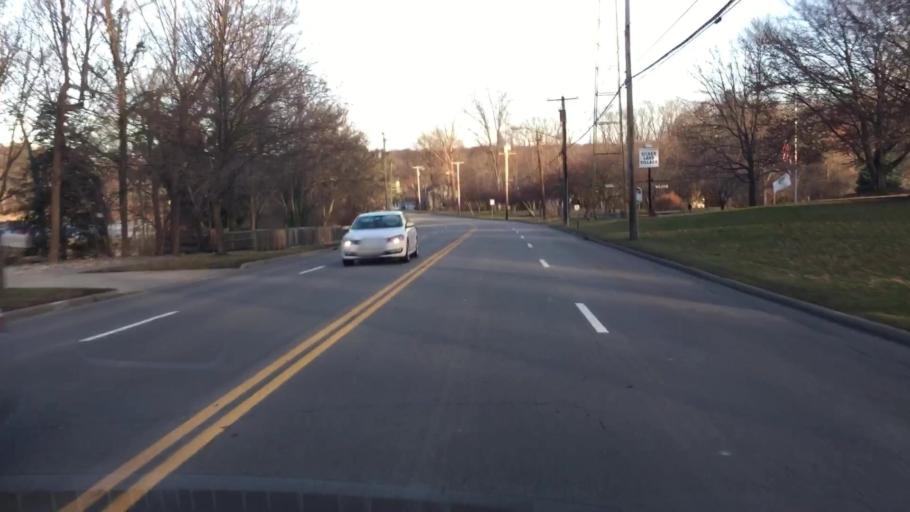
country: US
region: Ohio
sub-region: Summit County
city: Silver Lake
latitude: 41.1514
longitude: -81.4587
